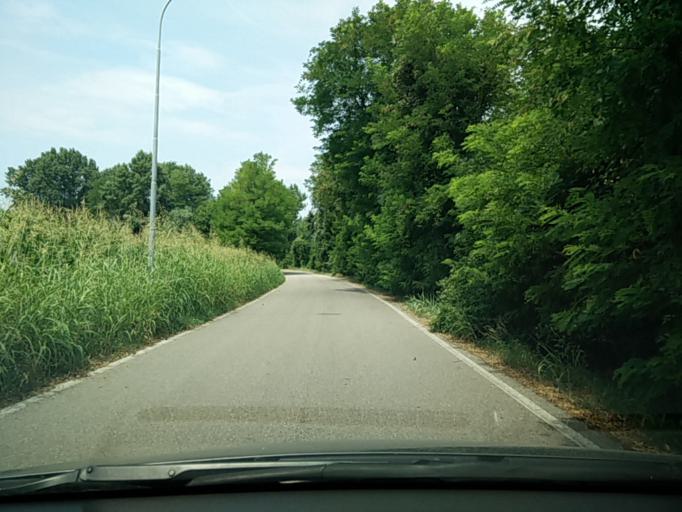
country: IT
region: Veneto
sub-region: Provincia di Treviso
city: Casier
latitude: 45.6502
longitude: 12.2884
